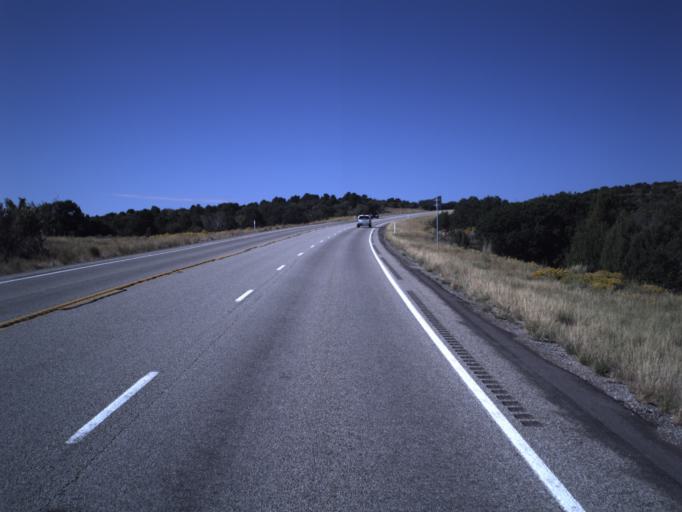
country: US
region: Utah
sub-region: San Juan County
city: Monticello
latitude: 37.7762
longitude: -109.3548
